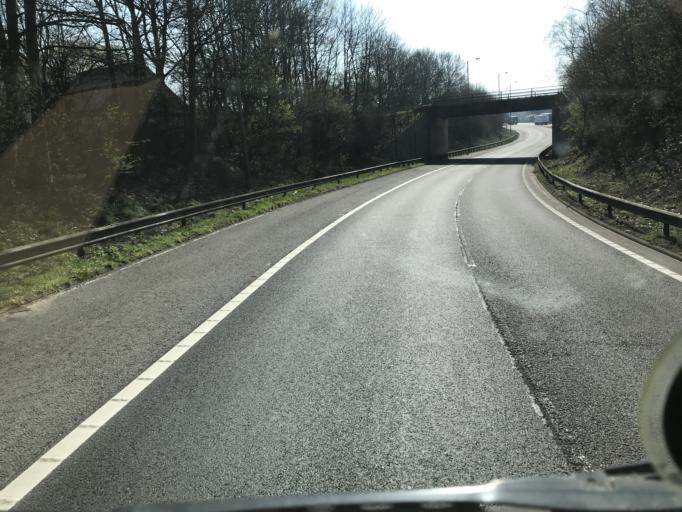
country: GB
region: England
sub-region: Warrington
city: Lymm
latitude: 53.3503
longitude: -2.4995
